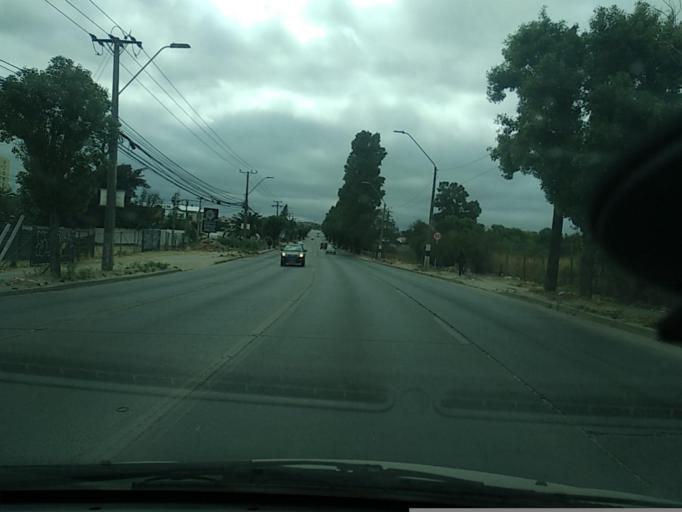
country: CL
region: Valparaiso
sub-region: Provincia de Marga Marga
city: Villa Alemana
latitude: -33.0462
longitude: -71.3980
